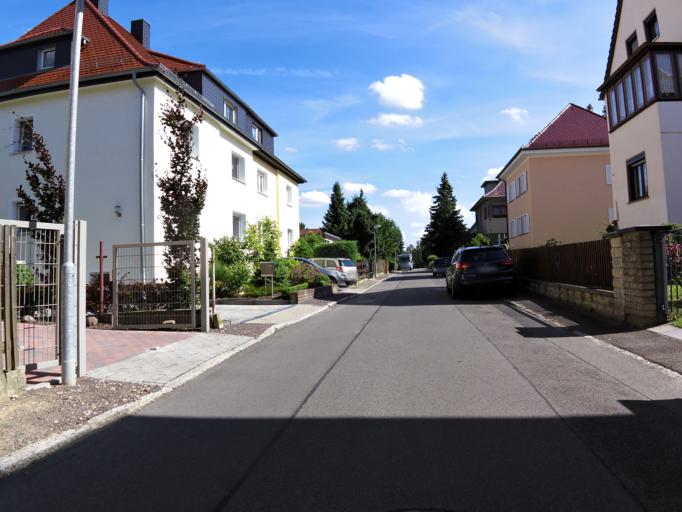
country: DE
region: Saxony
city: Leipzig
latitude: 51.3223
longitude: 12.4412
